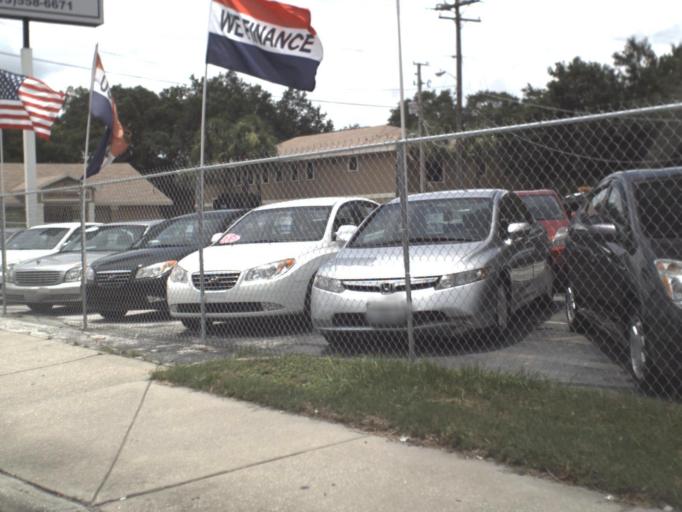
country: US
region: Florida
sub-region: Hillsborough County
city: University
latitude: 28.0693
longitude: -82.4528
